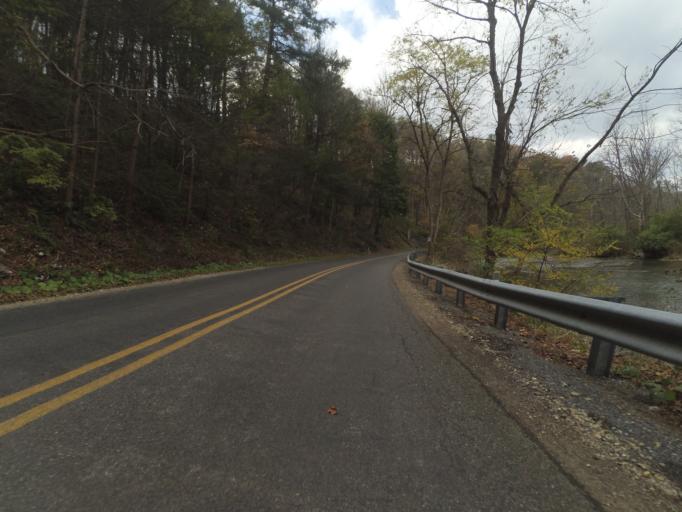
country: US
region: Pennsylvania
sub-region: Centre County
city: Bellefonte
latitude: 40.8936
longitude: -77.7936
